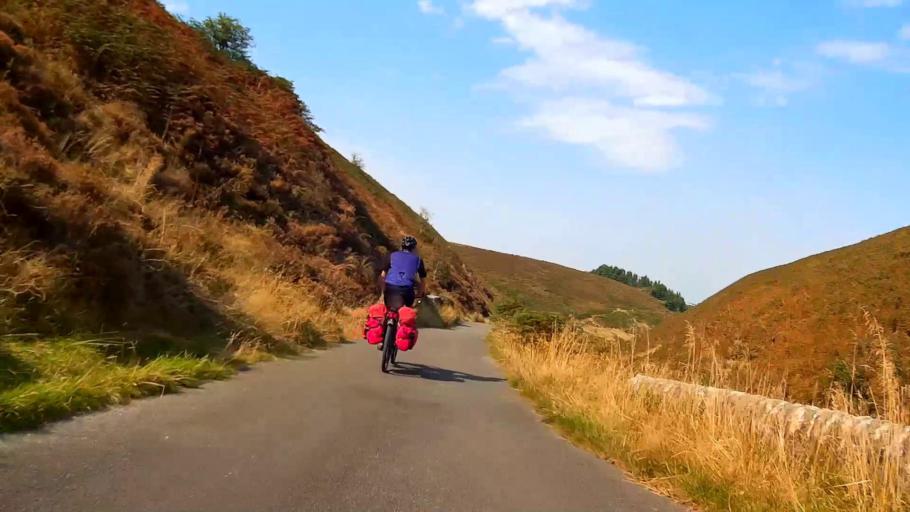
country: GB
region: England
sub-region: Derbyshire
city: Buxton
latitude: 53.2467
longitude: -1.9759
